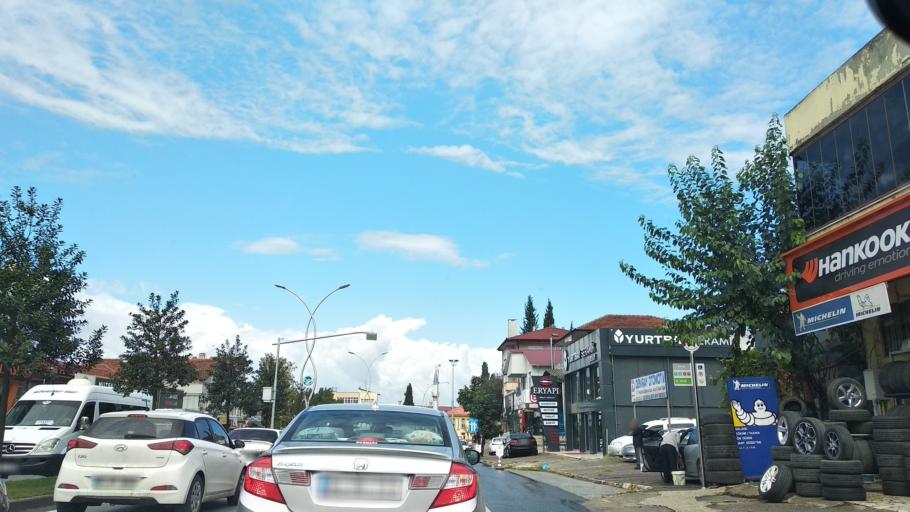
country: TR
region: Sakarya
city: Adapazari
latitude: 40.7530
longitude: 30.3838
